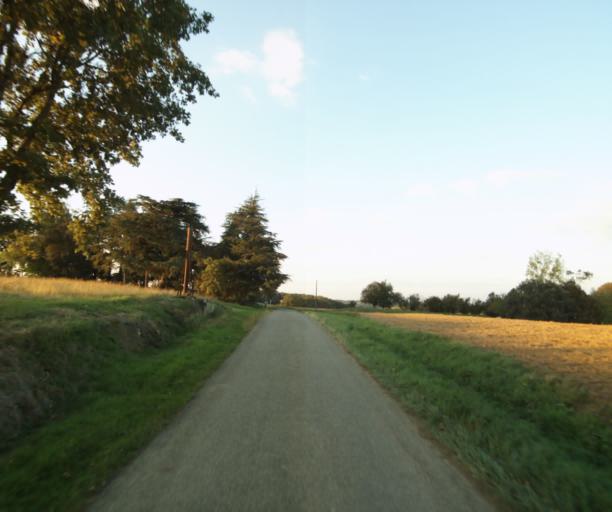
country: FR
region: Midi-Pyrenees
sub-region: Departement du Gers
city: Vic-Fezensac
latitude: 43.7673
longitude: 0.1947
